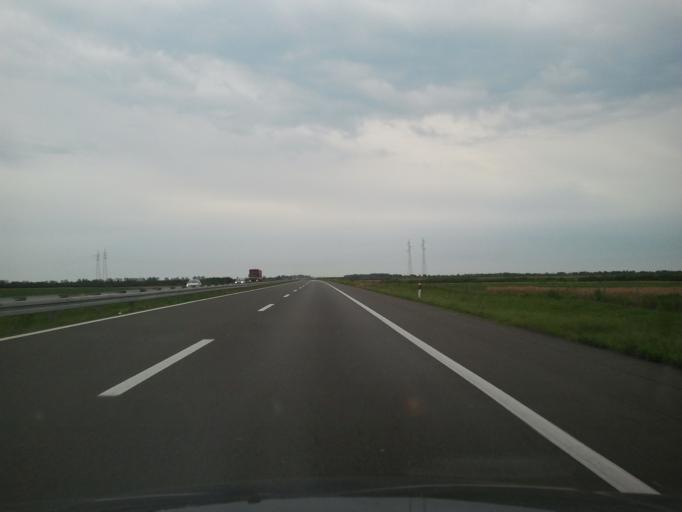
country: RS
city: Sasinci
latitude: 44.9702
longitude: 19.7699
